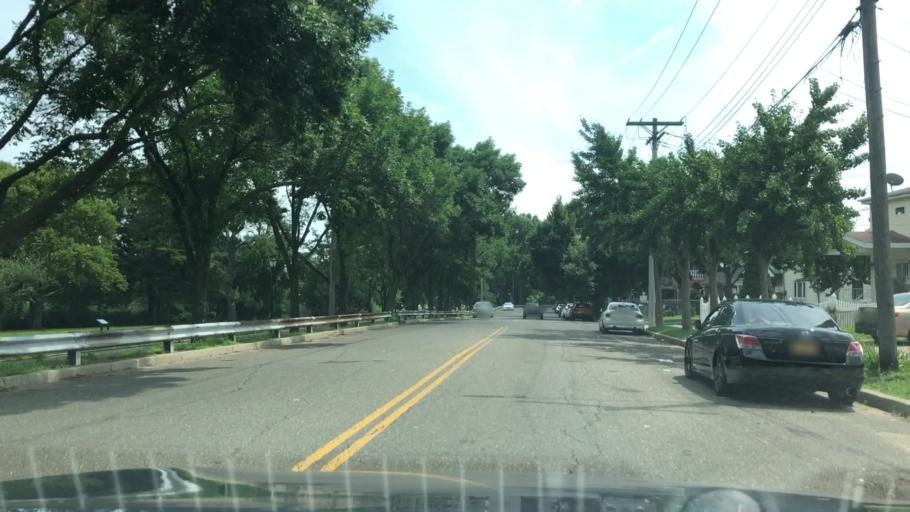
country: US
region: New York
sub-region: Queens County
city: Jamaica
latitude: 40.6770
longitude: -73.7869
